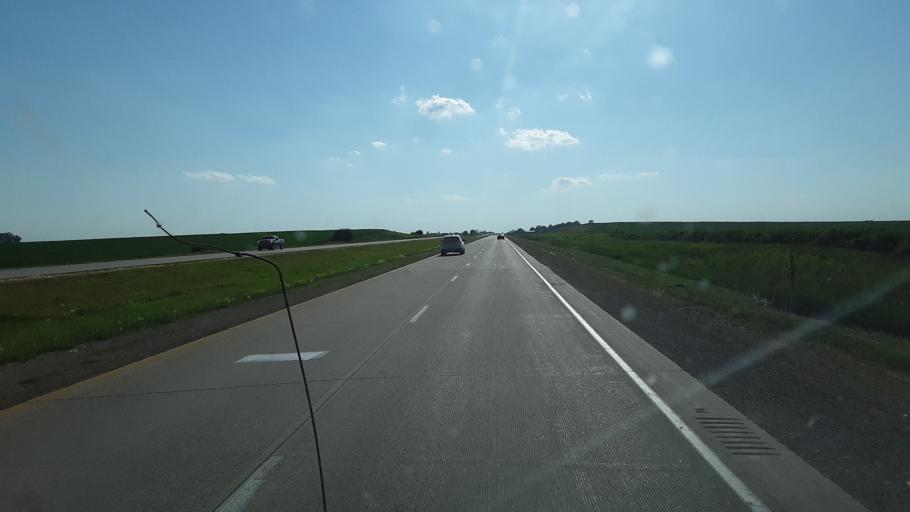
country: US
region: Iowa
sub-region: Grundy County
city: Dike
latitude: 42.4635
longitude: -92.7120
